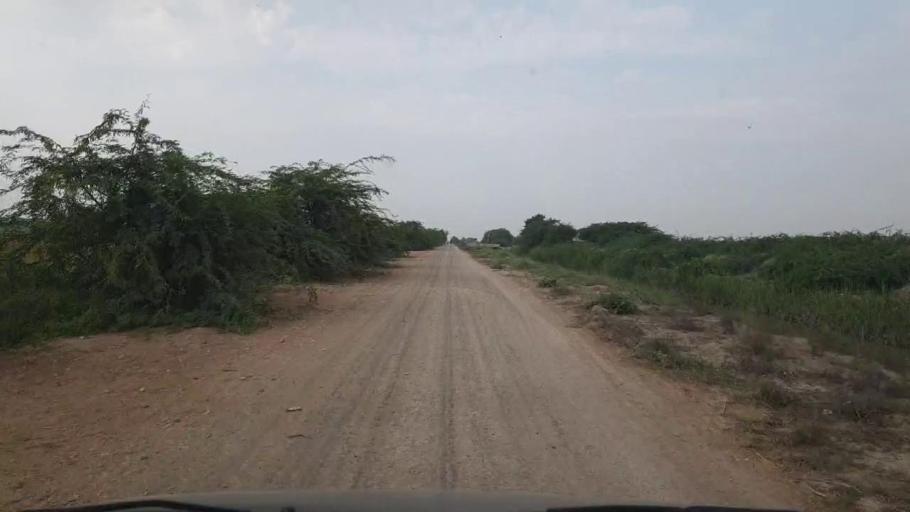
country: PK
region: Sindh
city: Kario
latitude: 24.6032
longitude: 68.6001
